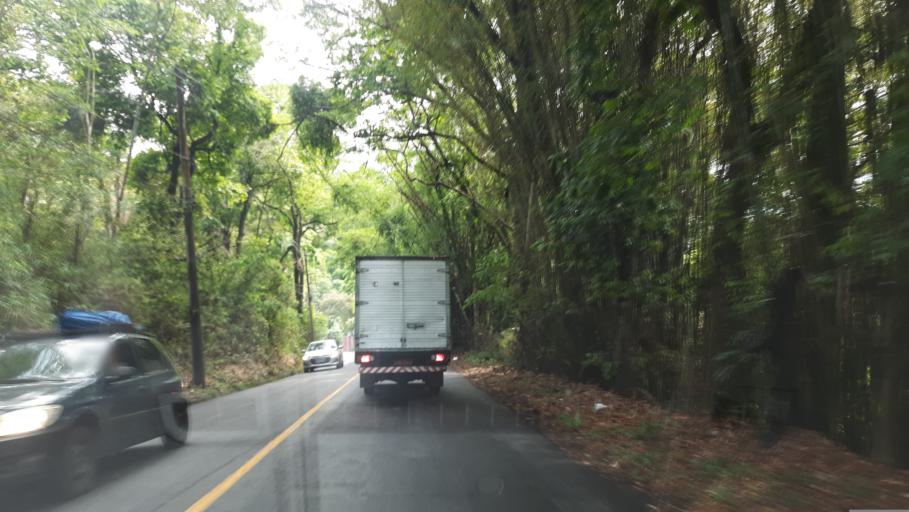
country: BR
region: Sao Paulo
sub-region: Caieiras
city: Caieiras
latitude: -23.3695
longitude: -46.6836
